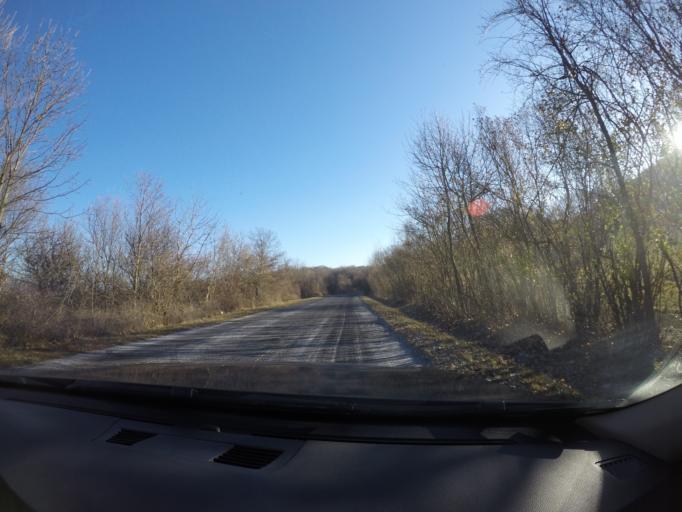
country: HU
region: Pest
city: Visegrad
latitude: 47.8000
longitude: 18.9921
